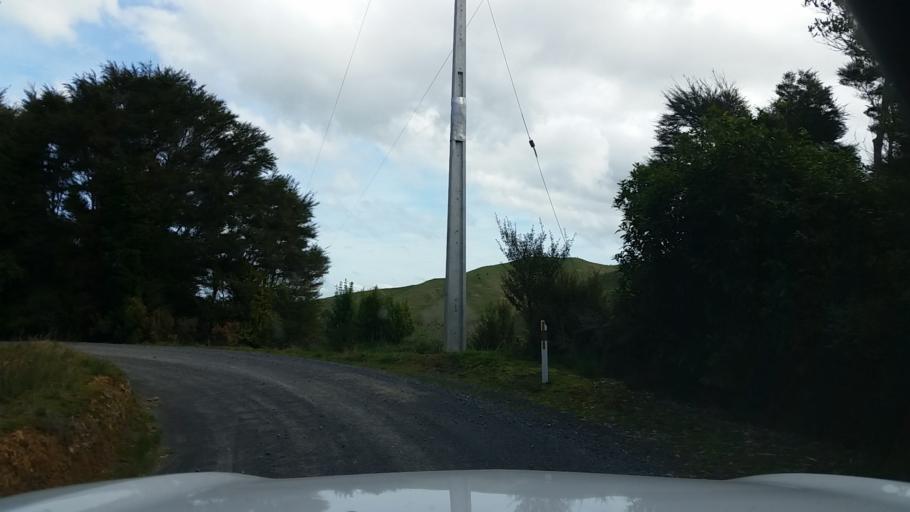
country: NZ
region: Waikato
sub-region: Hauraki District
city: Ngatea
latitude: -37.4822
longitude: 175.4521
